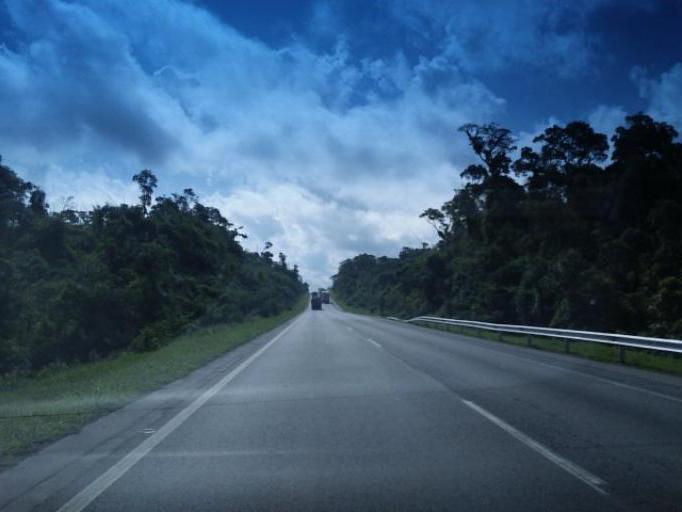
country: BR
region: Parana
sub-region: Antonina
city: Antonina
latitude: -25.1086
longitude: -48.7683
